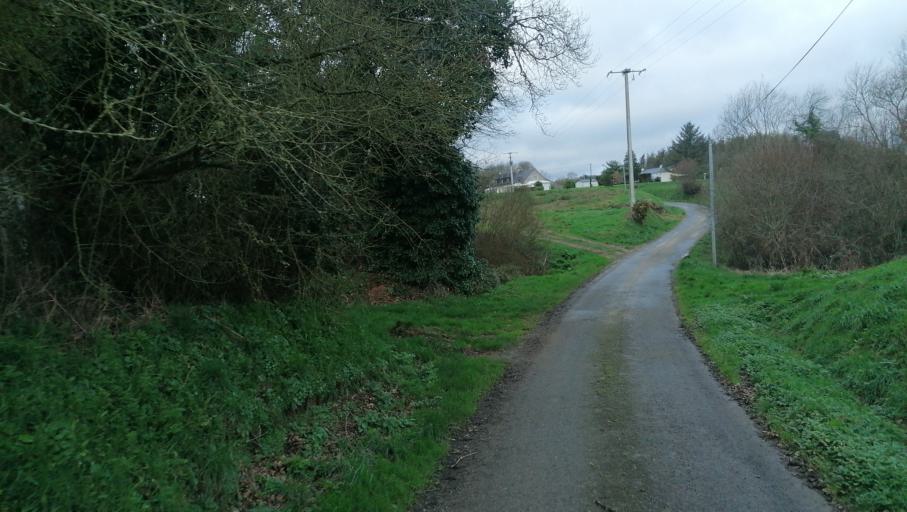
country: FR
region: Brittany
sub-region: Departement des Cotes-d'Armor
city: Pommerit-le-Vicomte
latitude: 48.6466
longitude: -3.0749
